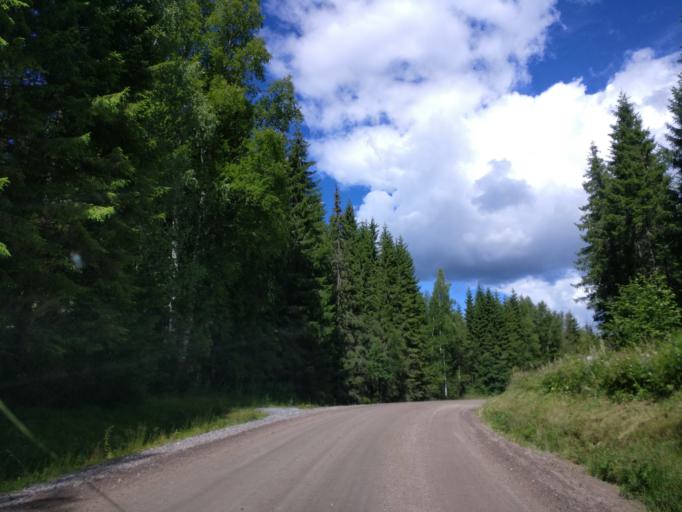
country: SE
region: Vaermland
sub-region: Hagfors Kommun
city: Ekshaerad
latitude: 60.0532
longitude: 13.4793
